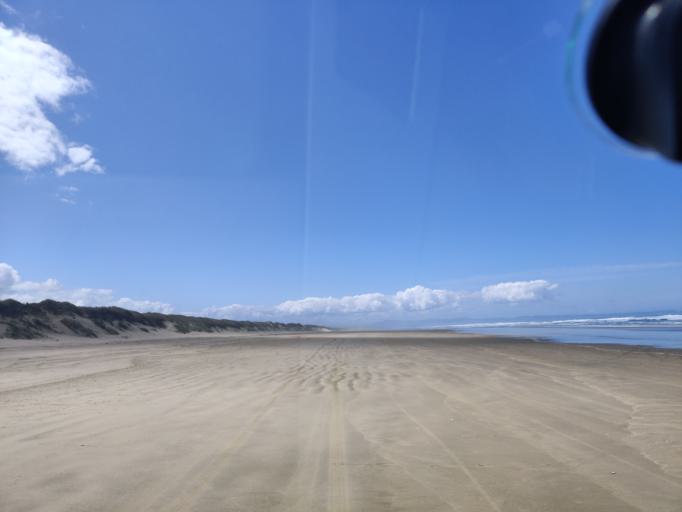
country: NZ
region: Northland
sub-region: Far North District
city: Kaitaia
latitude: -34.9414
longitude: 173.1157
